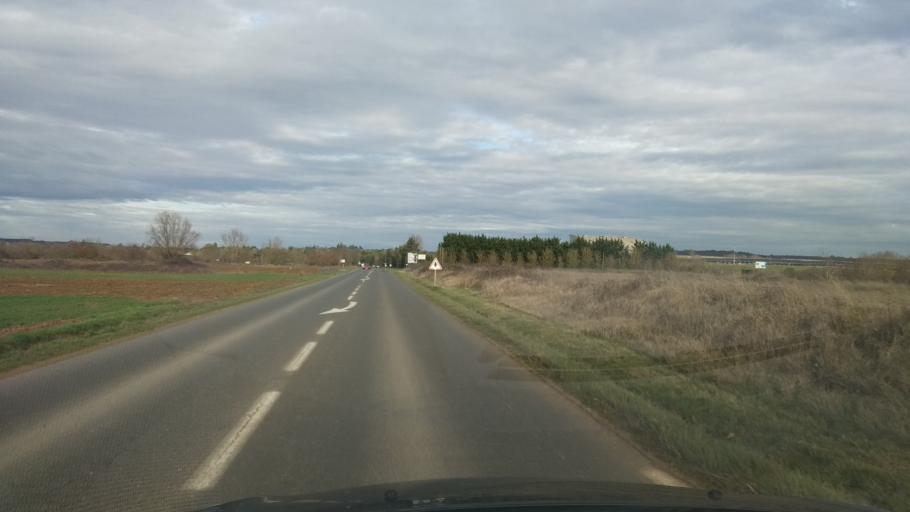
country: FR
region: Poitou-Charentes
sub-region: Departement de la Vienne
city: Saint-Georges-les-Baillargeaux
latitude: 46.6819
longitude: 0.4113
